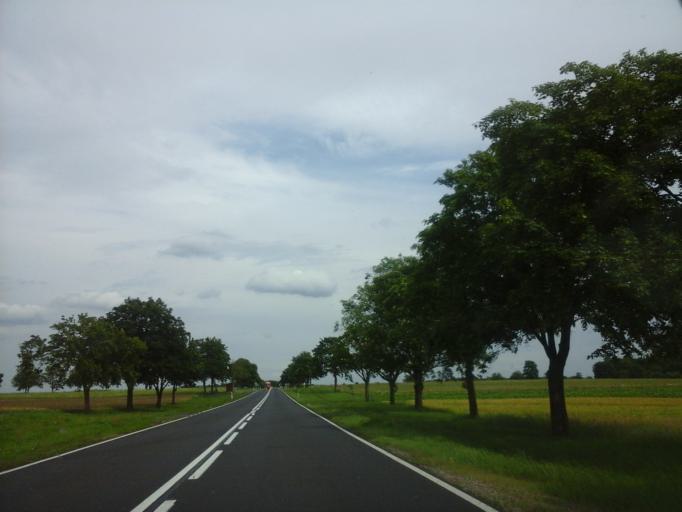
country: PL
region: West Pomeranian Voivodeship
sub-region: Powiat stargardzki
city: Suchan
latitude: 53.2769
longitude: 15.3568
